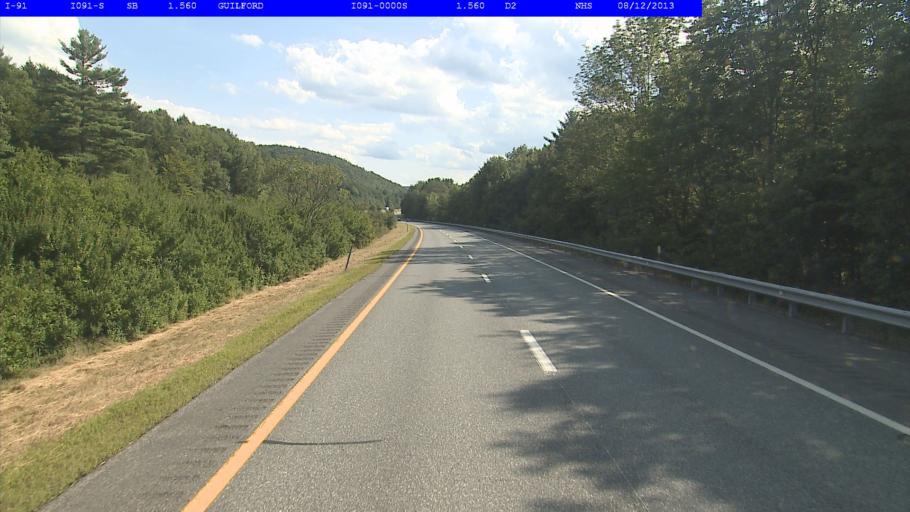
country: US
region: Massachusetts
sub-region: Franklin County
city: Bernardston
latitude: 42.7525
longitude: -72.5667
